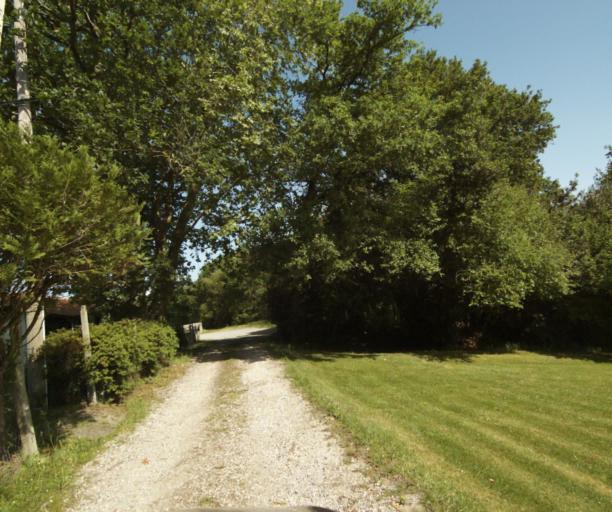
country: FR
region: Aquitaine
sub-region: Departement des Pyrenees-Atlantiques
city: Villefranque
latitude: 43.4626
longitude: -1.4485
